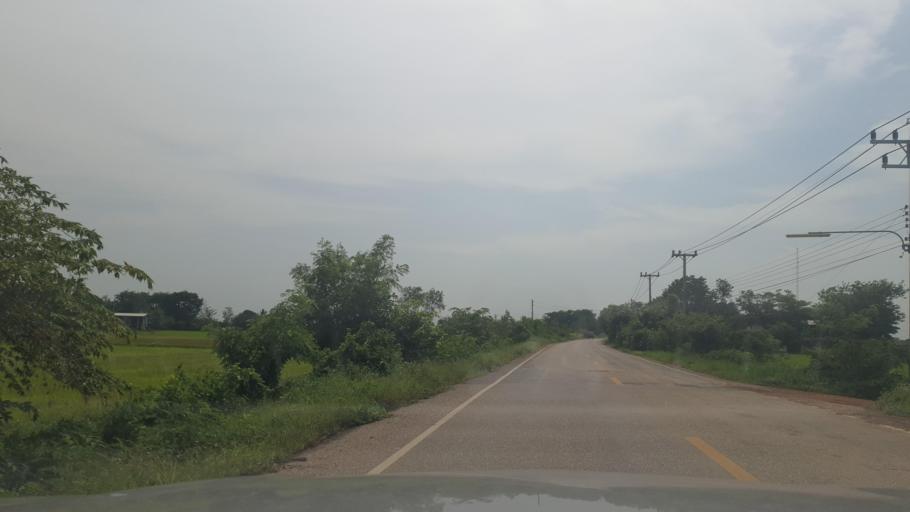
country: TH
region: Sukhothai
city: Si Samrong
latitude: 17.1163
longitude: 99.8808
